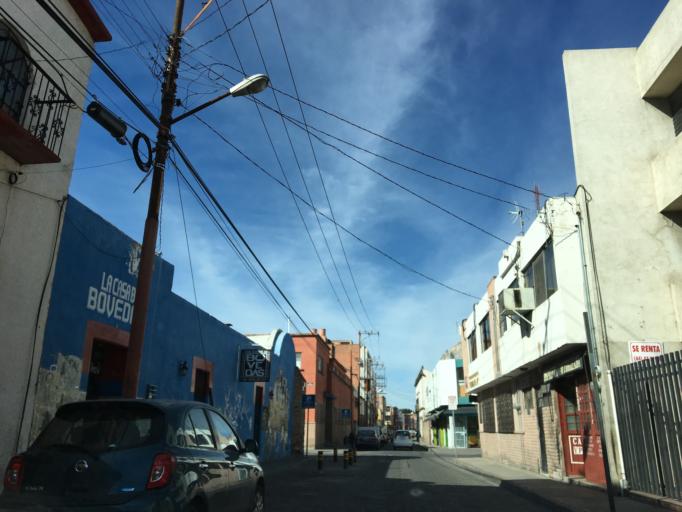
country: MX
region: San Luis Potosi
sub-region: San Luis Potosi
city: San Luis Potosi
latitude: 22.1501
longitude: -100.9811
